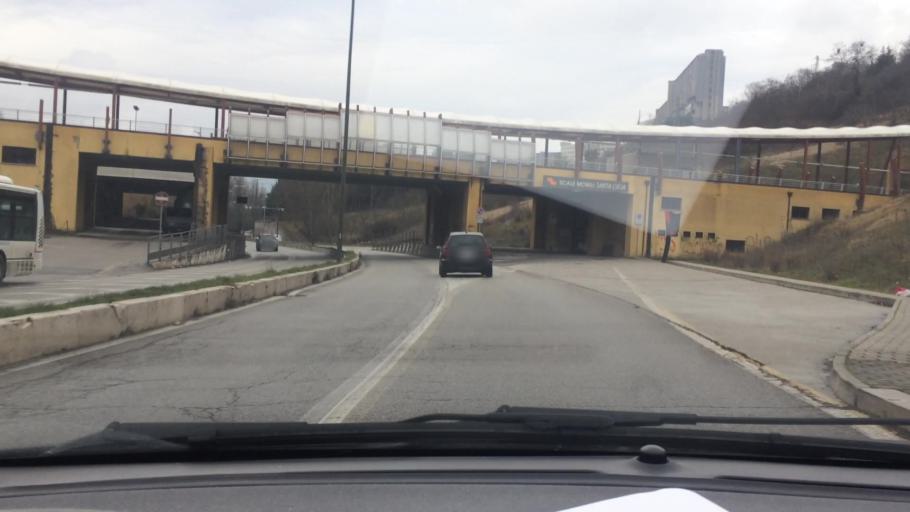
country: IT
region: Basilicate
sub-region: Provincia di Potenza
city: Potenza
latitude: 40.6375
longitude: 15.7956
